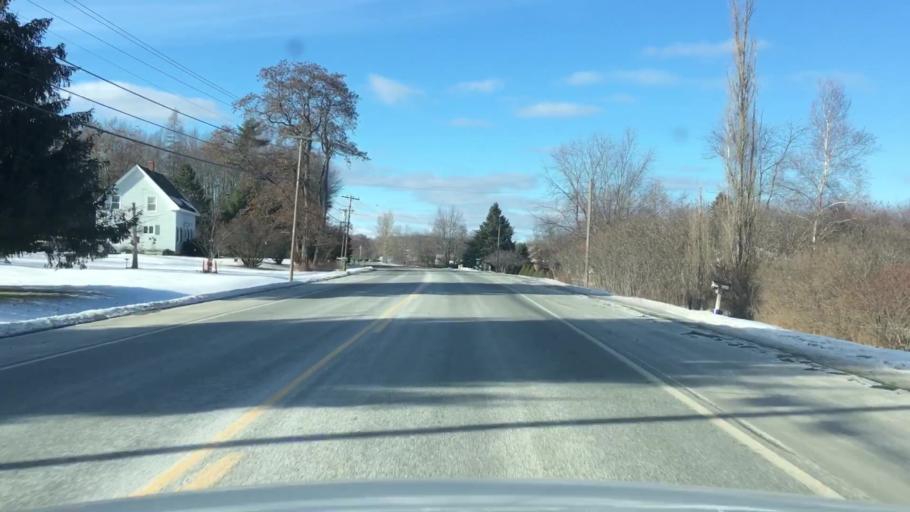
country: US
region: Maine
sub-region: Penobscot County
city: Eddington
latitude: 44.8217
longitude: -68.6496
